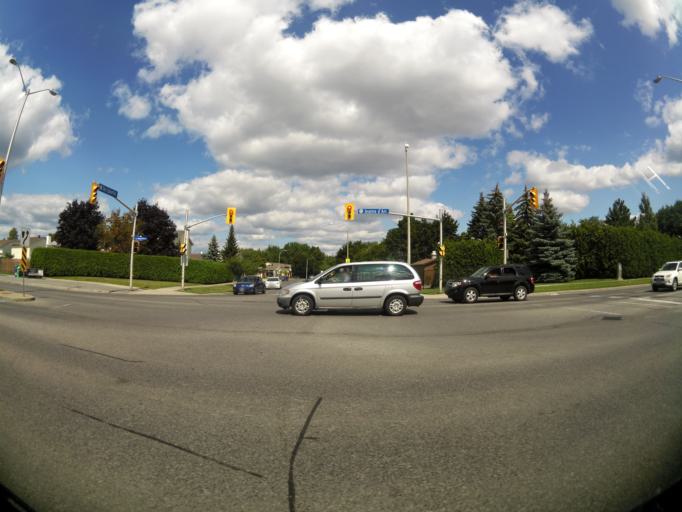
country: CA
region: Quebec
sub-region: Outaouais
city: Gatineau
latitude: 45.4592
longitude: -75.5101
